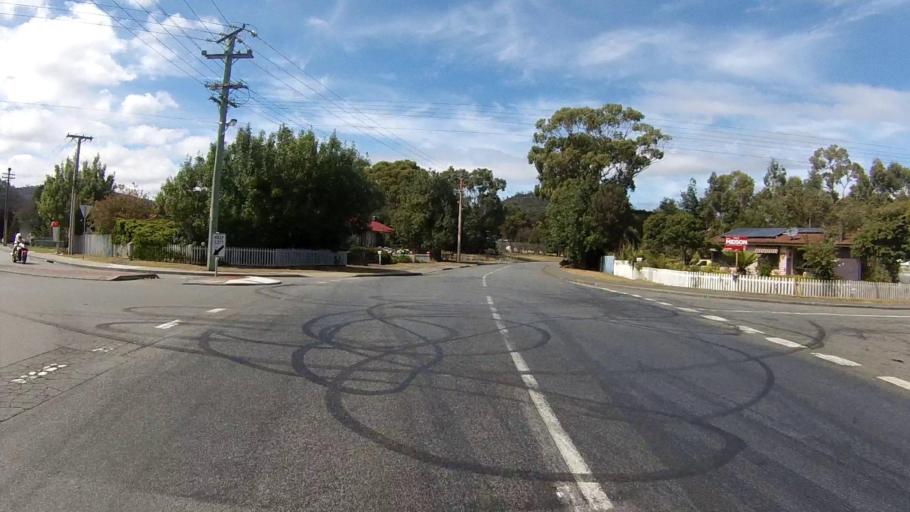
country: AU
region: Tasmania
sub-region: Clarence
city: Lindisfarne
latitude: -42.8094
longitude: 147.3506
